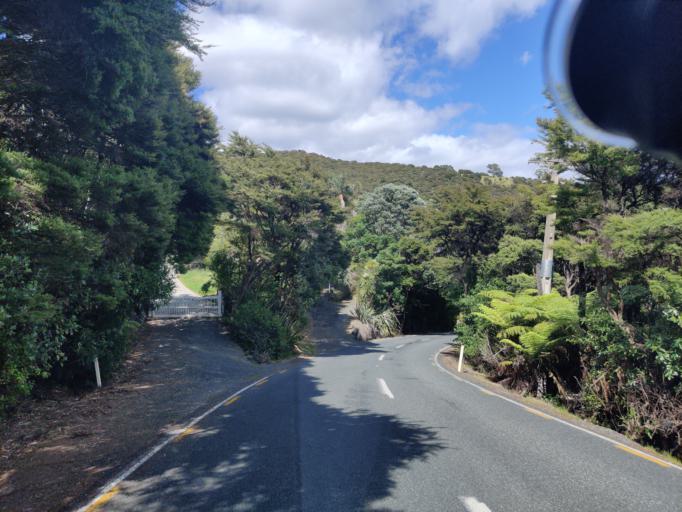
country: NZ
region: Northland
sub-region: Far North District
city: Paihia
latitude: -35.2570
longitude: 174.2445
